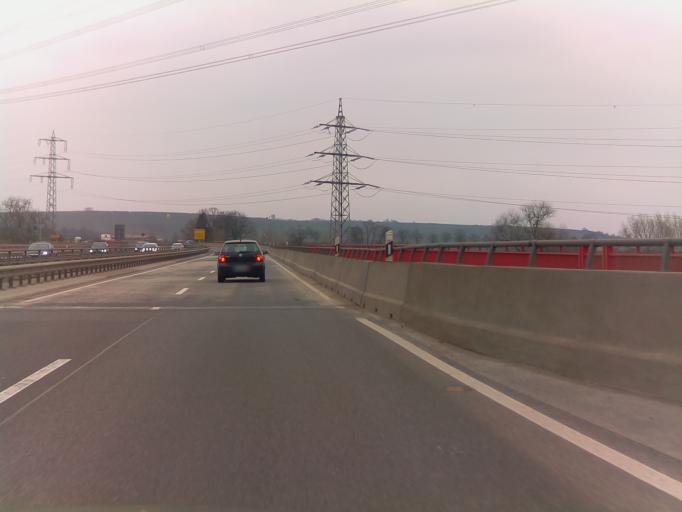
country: DE
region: Rheinland-Pfalz
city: Bretzenheim
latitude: 49.8626
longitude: 7.8887
